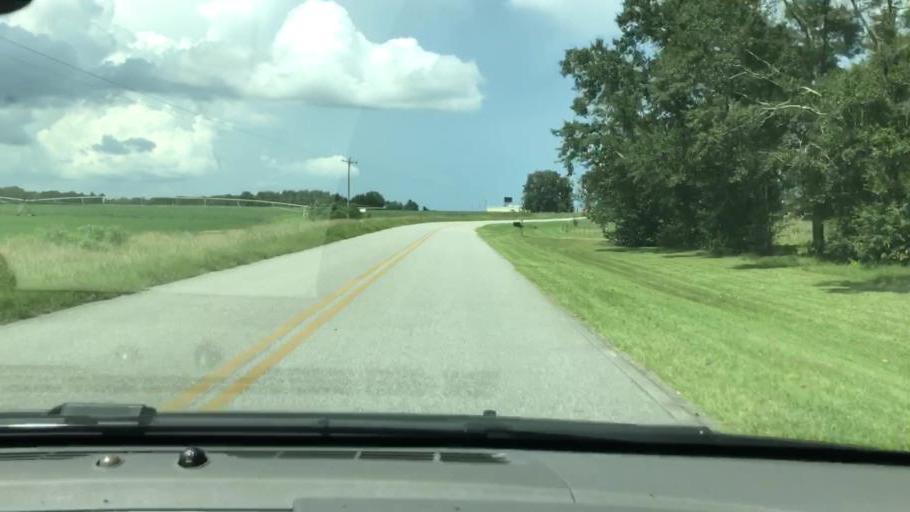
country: US
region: Georgia
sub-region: Seminole County
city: Donalsonville
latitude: 31.0859
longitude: -84.9960
